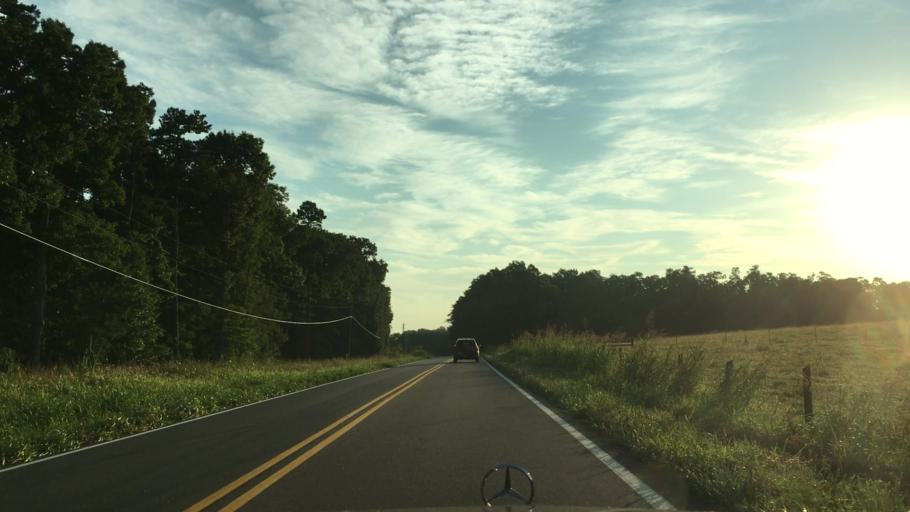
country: US
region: Virginia
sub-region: Campbell County
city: Timberlake
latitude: 37.2903
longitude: -79.2367
